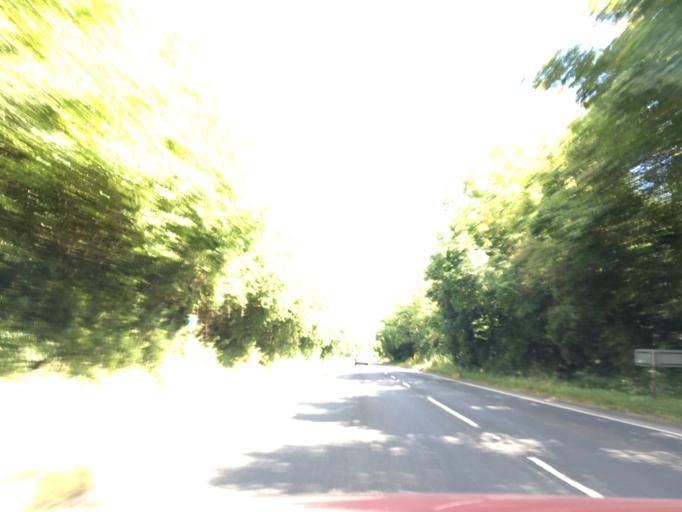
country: GB
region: England
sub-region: Dorset
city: Dorchester
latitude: 50.7354
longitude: -2.4697
